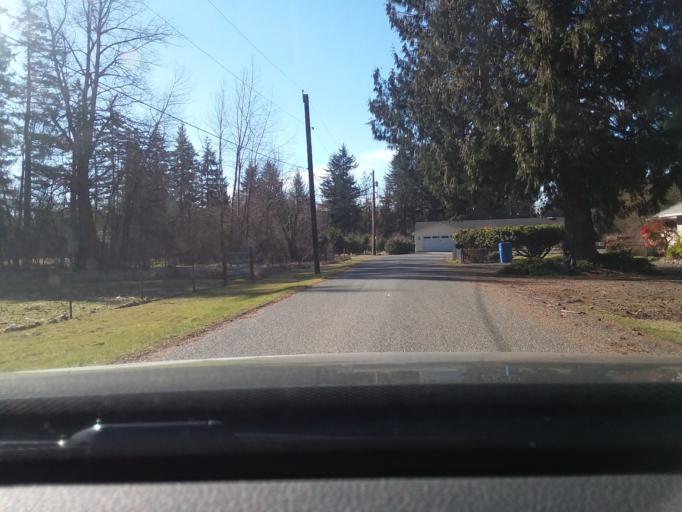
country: US
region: Washington
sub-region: Pierce County
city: Summit
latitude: 47.1288
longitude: -122.3507
